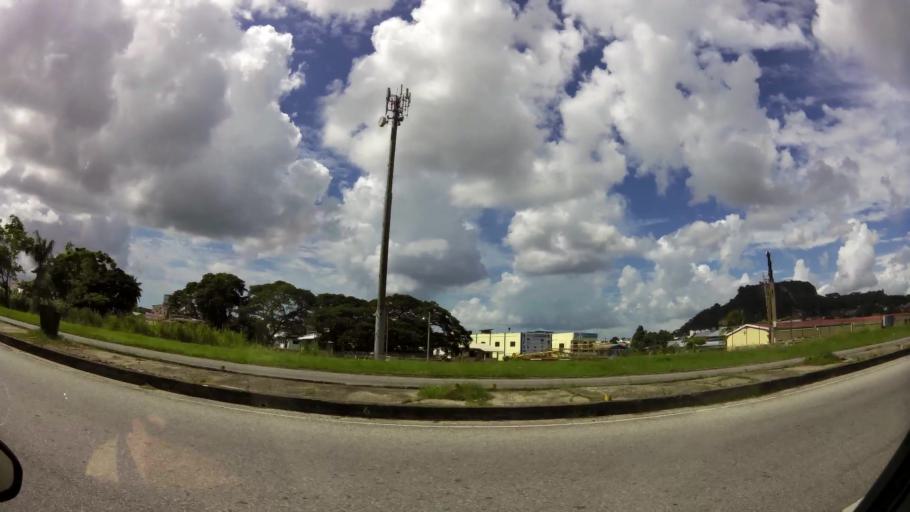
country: TT
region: City of San Fernando
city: Mon Repos
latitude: 10.2697
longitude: -61.4559
